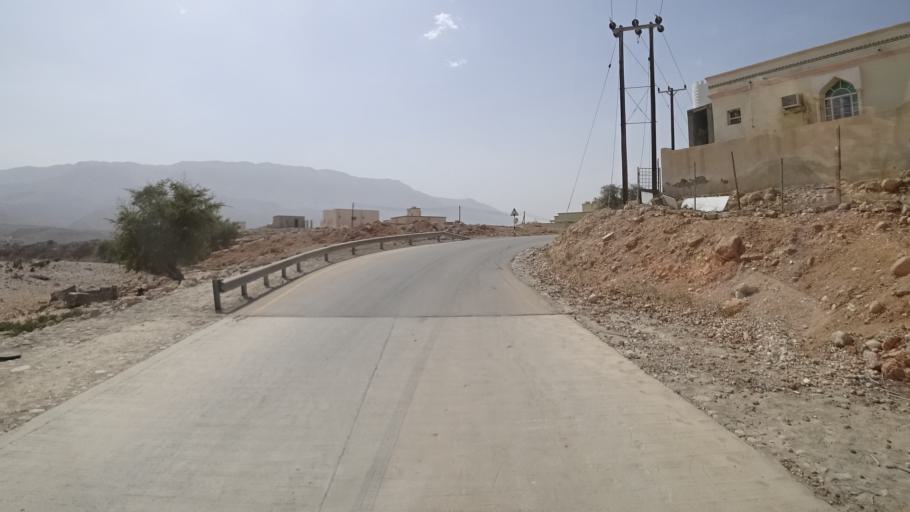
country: OM
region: Ash Sharqiyah
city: Sur
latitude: 22.9900
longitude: 59.1377
